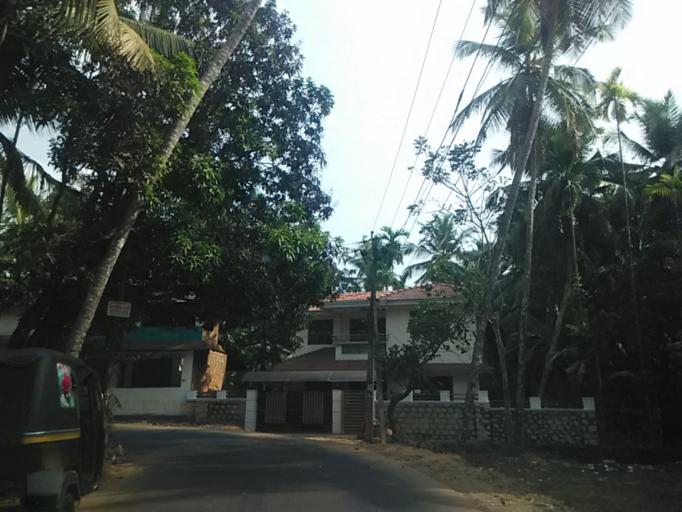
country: IN
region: Kerala
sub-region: Kozhikode
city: Naduvannur
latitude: 11.5805
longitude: 75.7169
